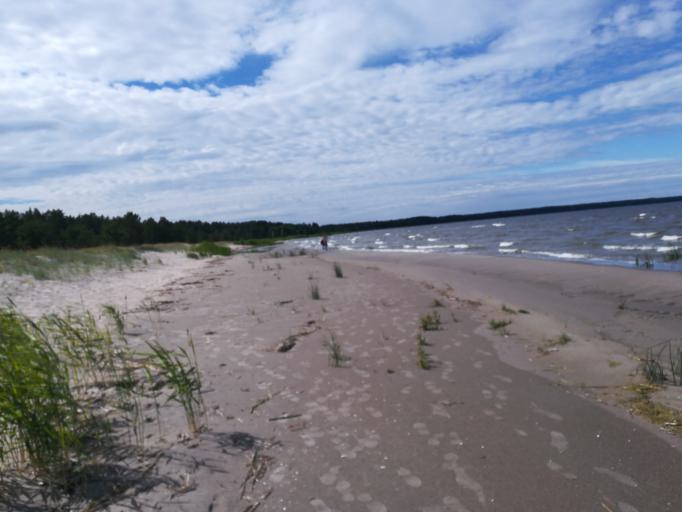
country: RU
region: Leningrad
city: Ust'-Luga
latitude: 59.6797
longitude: 28.2379
